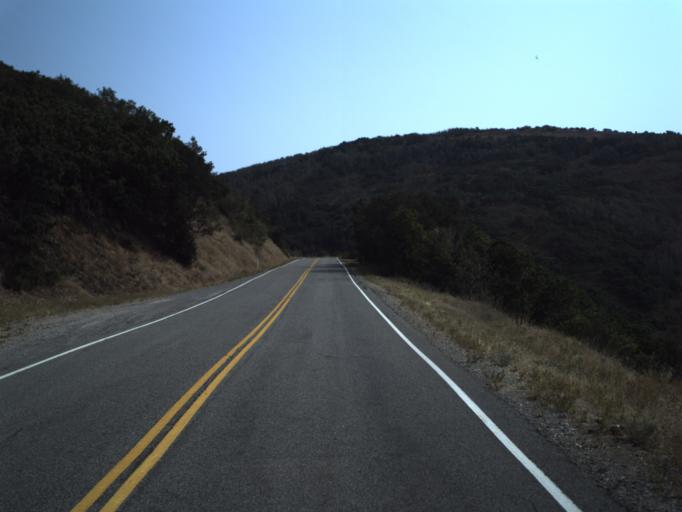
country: US
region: Utah
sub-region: Summit County
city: Summit Park
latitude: 40.8223
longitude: -111.6634
